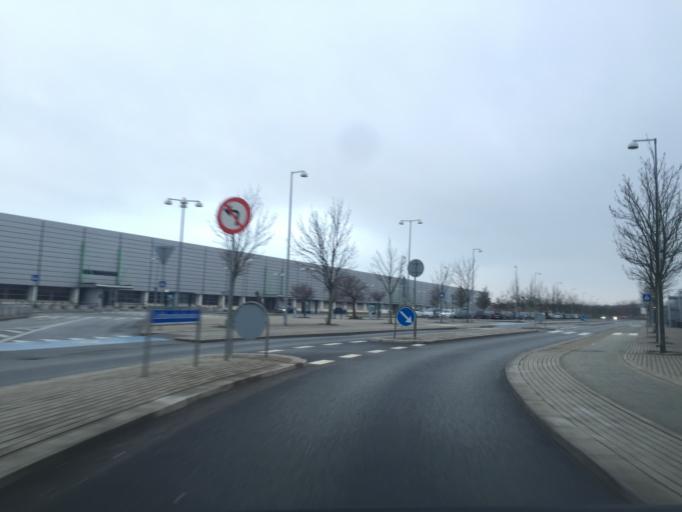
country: DK
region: Capital Region
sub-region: Tarnby Kommune
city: Tarnby
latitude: 55.6296
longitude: 12.6330
